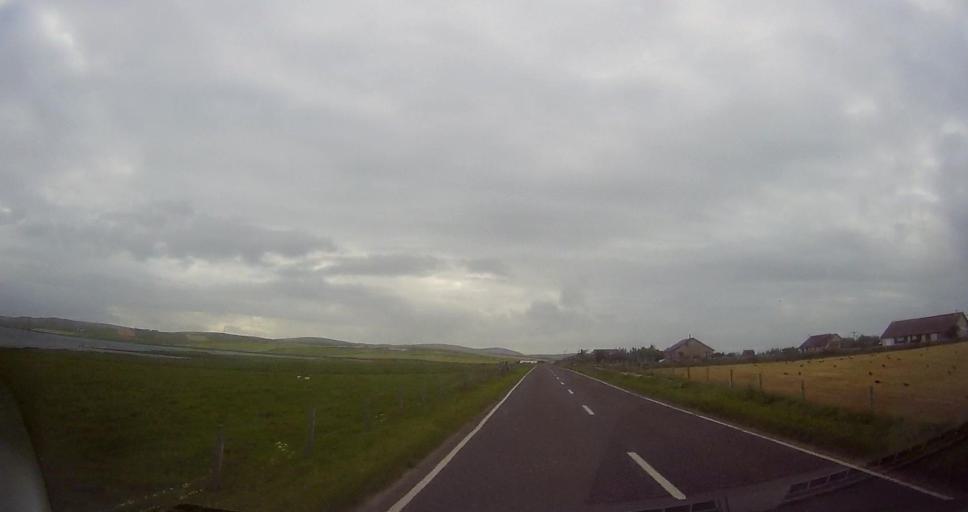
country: GB
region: Scotland
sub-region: Orkney Islands
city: Stromness
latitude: 58.9712
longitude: -3.2341
